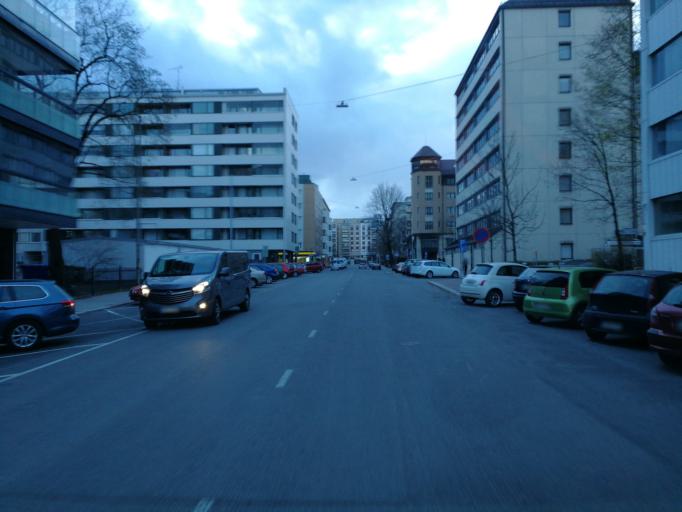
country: FI
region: Varsinais-Suomi
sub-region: Turku
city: Turku
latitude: 60.4480
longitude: 22.2572
